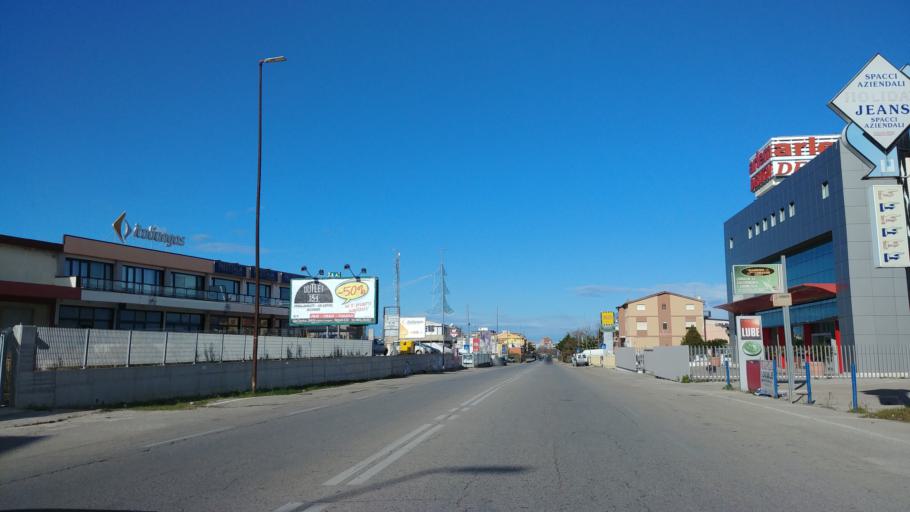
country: IT
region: Molise
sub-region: Provincia di Campobasso
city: Termoli
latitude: 41.9878
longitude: 15.0023
